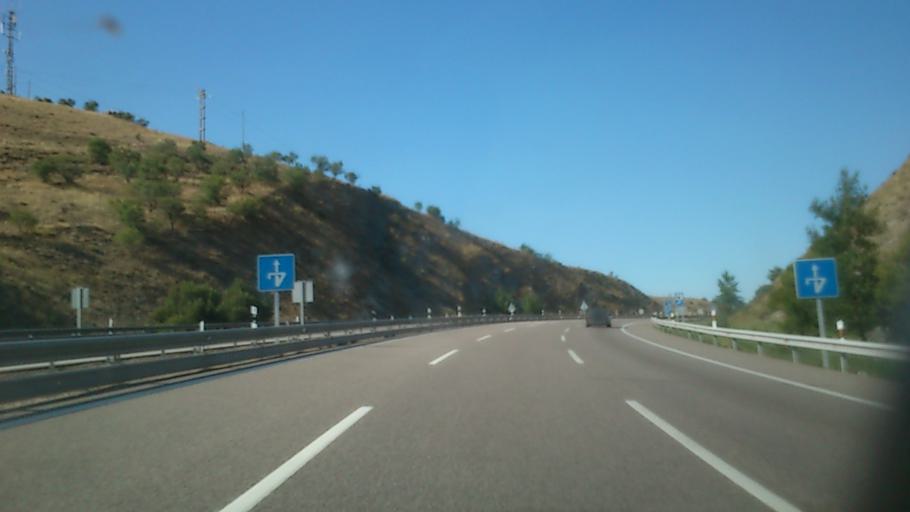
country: ES
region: Aragon
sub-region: Provincia de Zaragoza
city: Paracuellos de la Ribera
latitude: 41.4110
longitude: -1.5268
